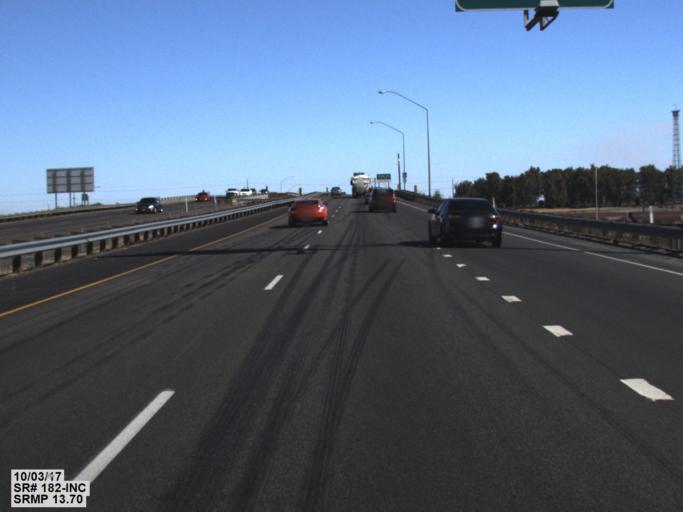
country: US
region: Washington
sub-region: Franklin County
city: Pasco
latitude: 46.2494
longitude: -119.0963
